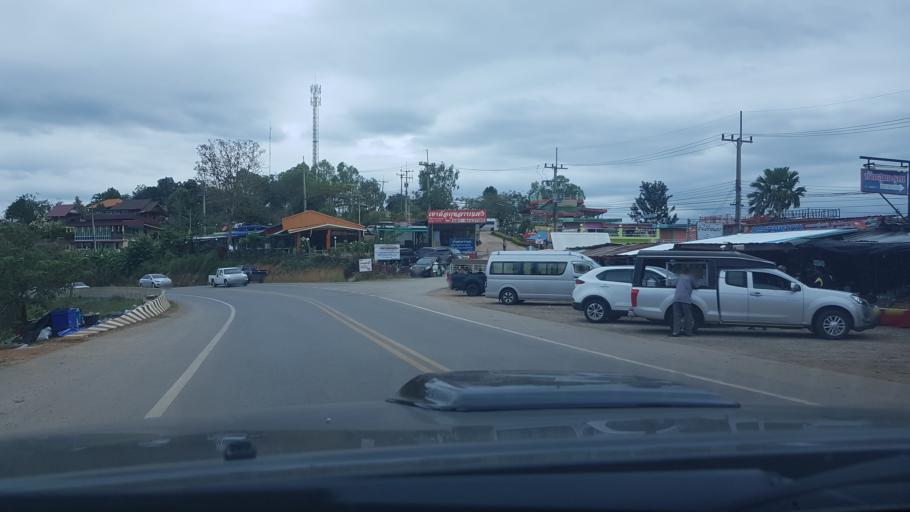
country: TH
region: Phetchabun
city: Khao Kho
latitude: 16.5690
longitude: 101.0060
